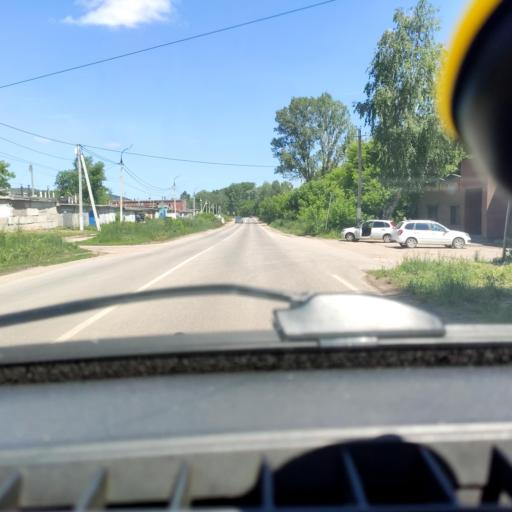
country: RU
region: Samara
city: Zhigulevsk
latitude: 53.3885
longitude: 49.5077
